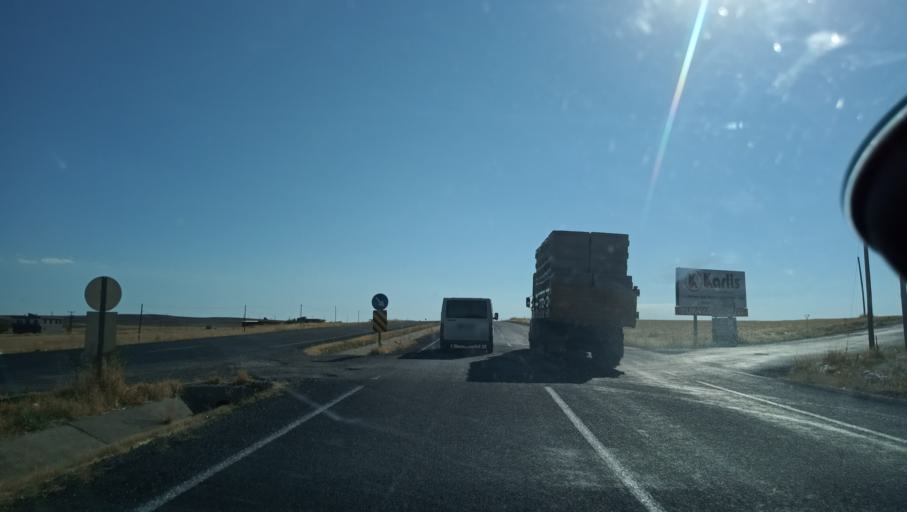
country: TR
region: Diyarbakir
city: Ambar
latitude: 37.9981
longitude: 40.4117
